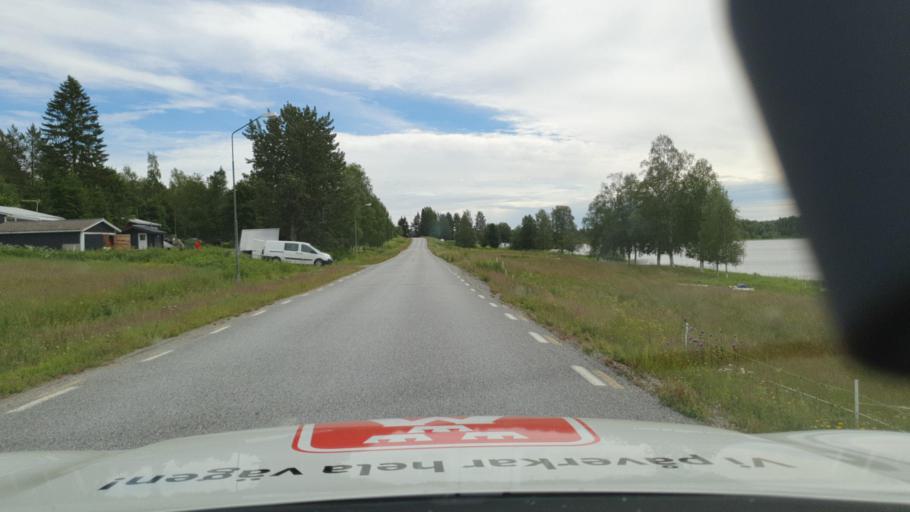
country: SE
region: Vaesterbotten
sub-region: Skelleftea Kommun
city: Burea
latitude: 64.4978
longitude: 21.0188
